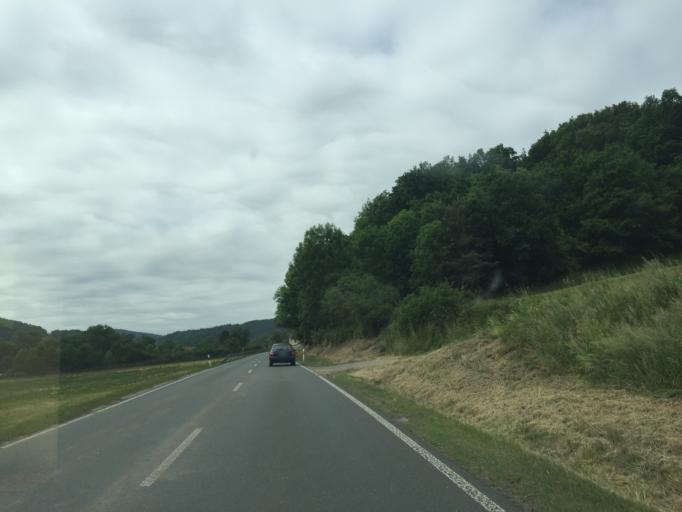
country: DE
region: Thuringia
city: Bad Blankenburg
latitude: 50.6881
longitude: 11.2446
